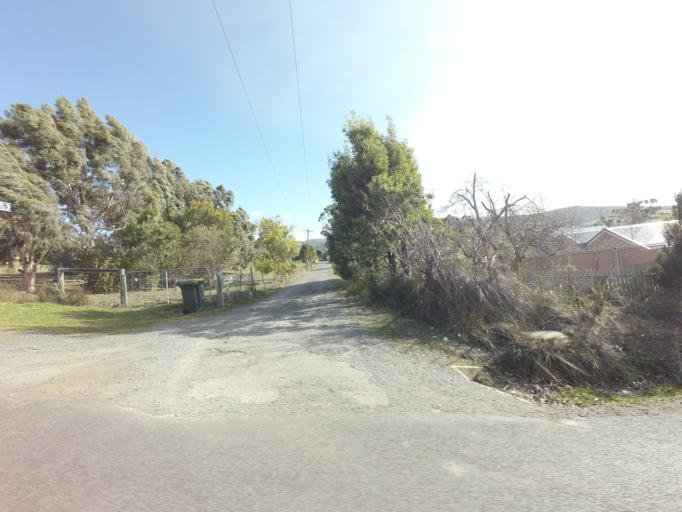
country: AU
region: Tasmania
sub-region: Kingborough
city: Margate
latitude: -43.0734
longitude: 147.2654
